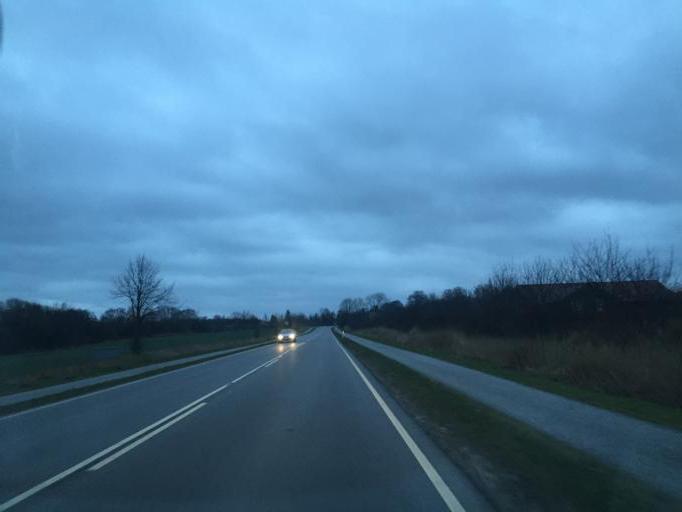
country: DK
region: South Denmark
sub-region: Haderslev Kommune
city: Starup
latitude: 55.2554
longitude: 9.5265
